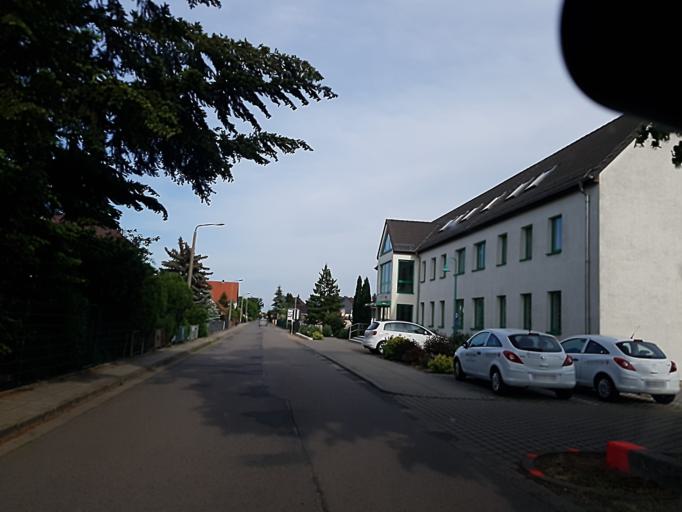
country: DE
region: Saxony-Anhalt
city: Jessen
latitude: 51.7907
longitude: 12.9592
